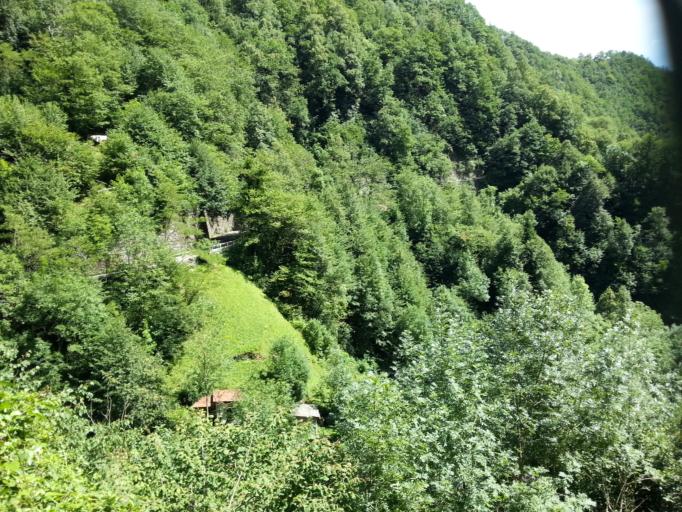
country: IT
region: Lombardy
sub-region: Provincia di Lecco
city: Pagnona
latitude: 46.0620
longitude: 9.4065
